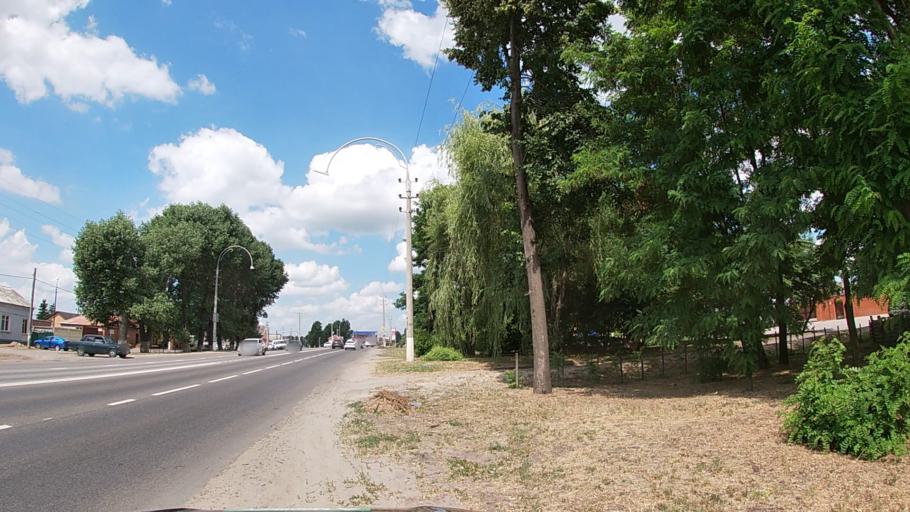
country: RU
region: Belgorod
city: Severnyy
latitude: 50.6262
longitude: 36.4968
